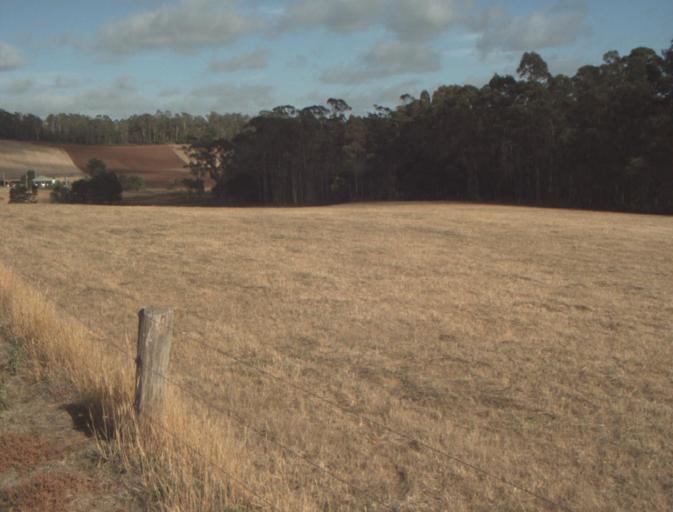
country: AU
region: Tasmania
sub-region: Dorset
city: Bridport
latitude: -41.1255
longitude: 147.2060
